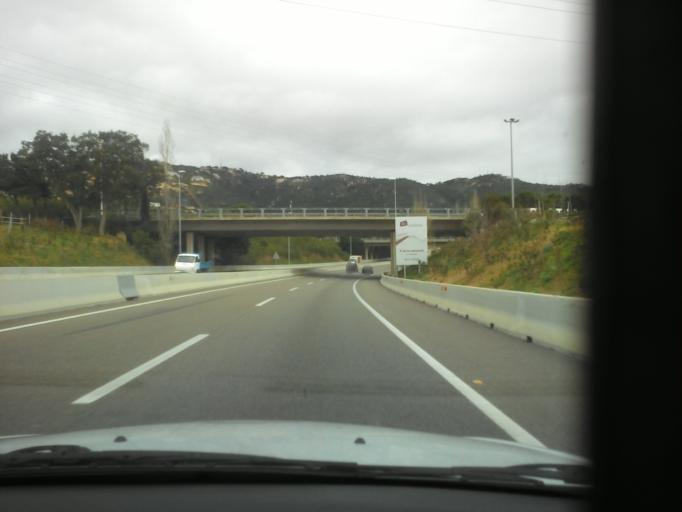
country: ES
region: Catalonia
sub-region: Provincia de Girona
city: Castell-Platja d'Aro
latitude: 41.8136
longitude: 3.0413
